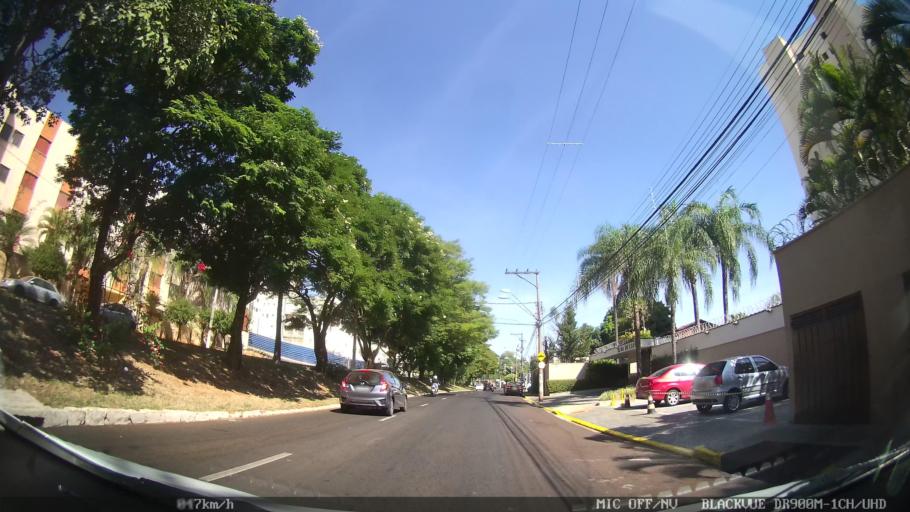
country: BR
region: Sao Paulo
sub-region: Ribeirao Preto
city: Ribeirao Preto
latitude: -21.1896
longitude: -47.8202
